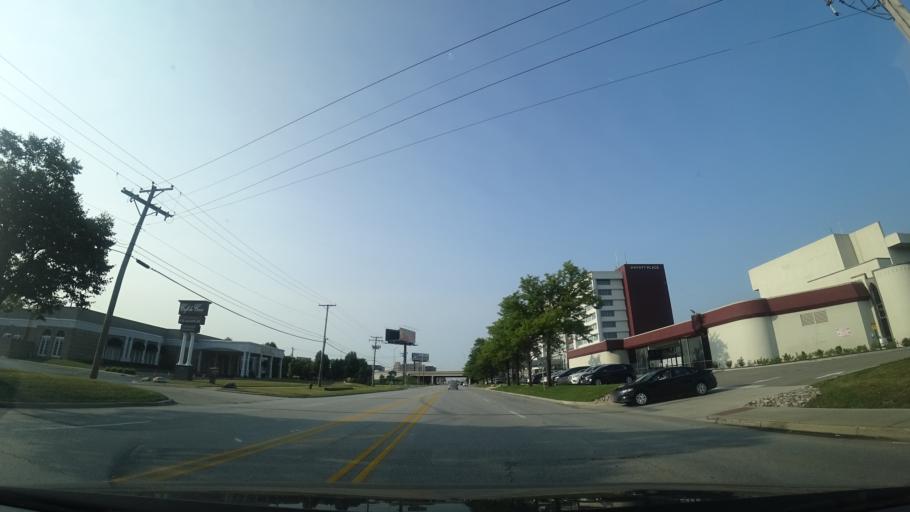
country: US
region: Illinois
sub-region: Cook County
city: Rosemont
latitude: 42.0034
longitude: -87.8846
